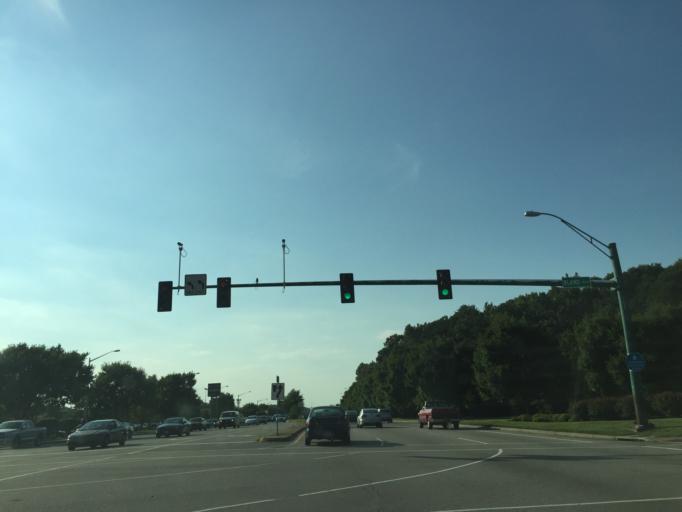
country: US
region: Virginia
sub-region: York County
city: Yorktown
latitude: 37.1278
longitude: -76.5115
